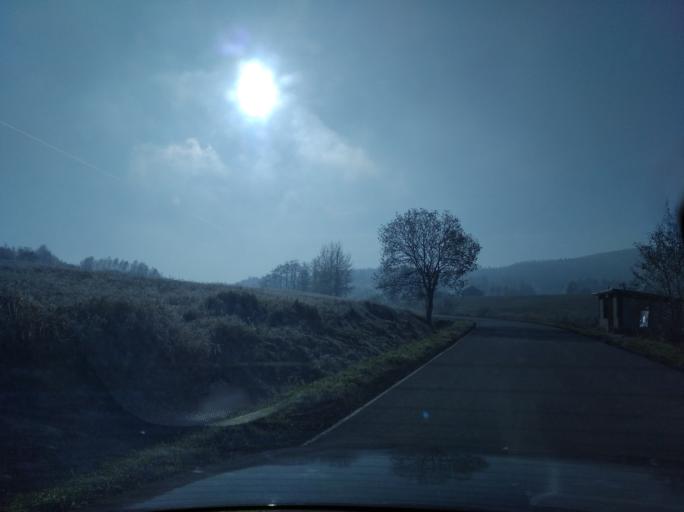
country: PL
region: Subcarpathian Voivodeship
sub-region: Powiat strzyzowski
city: Wysoka Strzyzowska
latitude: 49.8488
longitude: 21.7008
